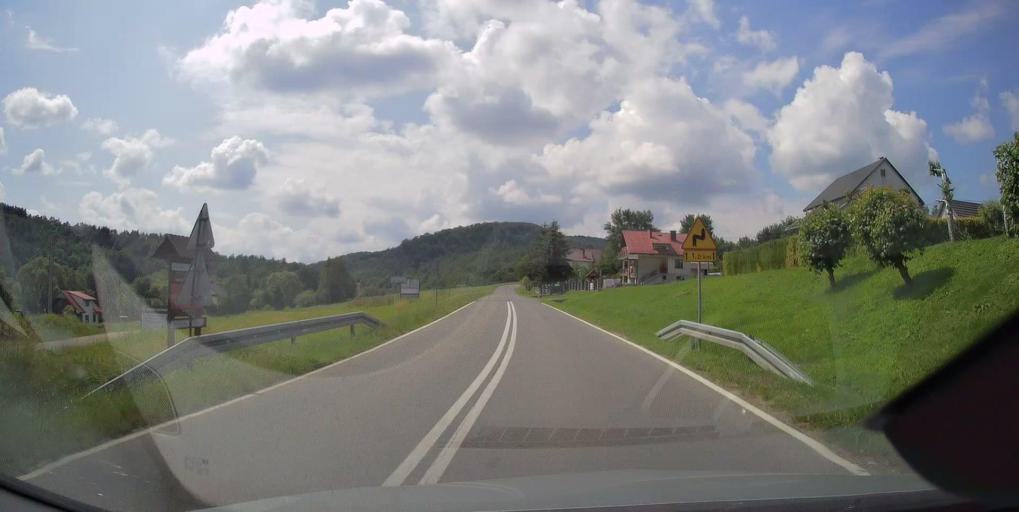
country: PL
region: Lesser Poland Voivodeship
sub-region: Powiat tarnowski
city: Zakliczyn
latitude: 49.7901
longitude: 20.7956
